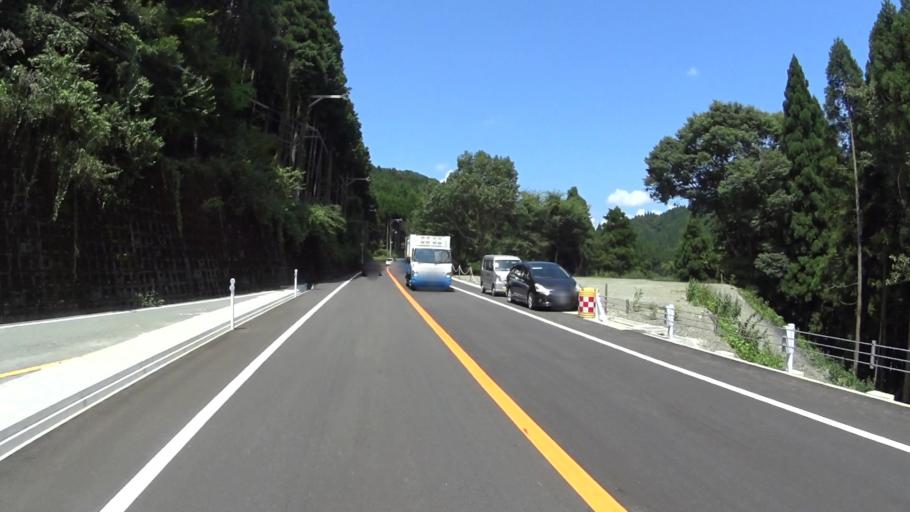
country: JP
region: Shiga Prefecture
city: Kitahama
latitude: 35.3601
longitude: 135.9186
